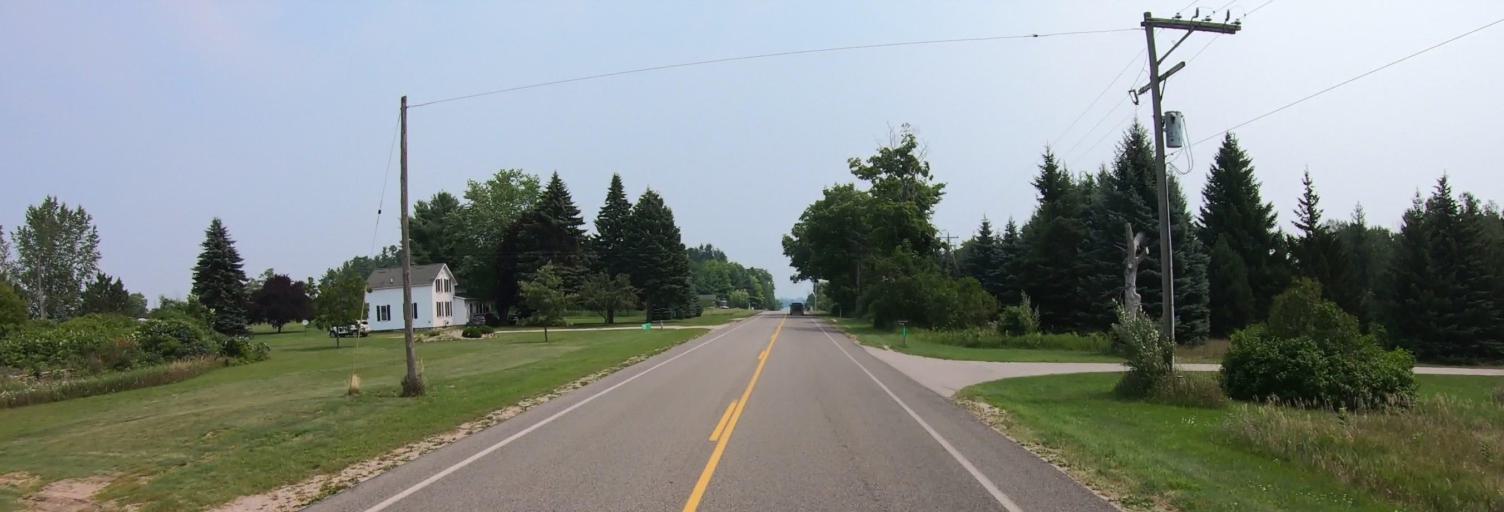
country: US
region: Michigan
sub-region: Leelanau County
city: Leland
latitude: 45.1509
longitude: -85.6072
